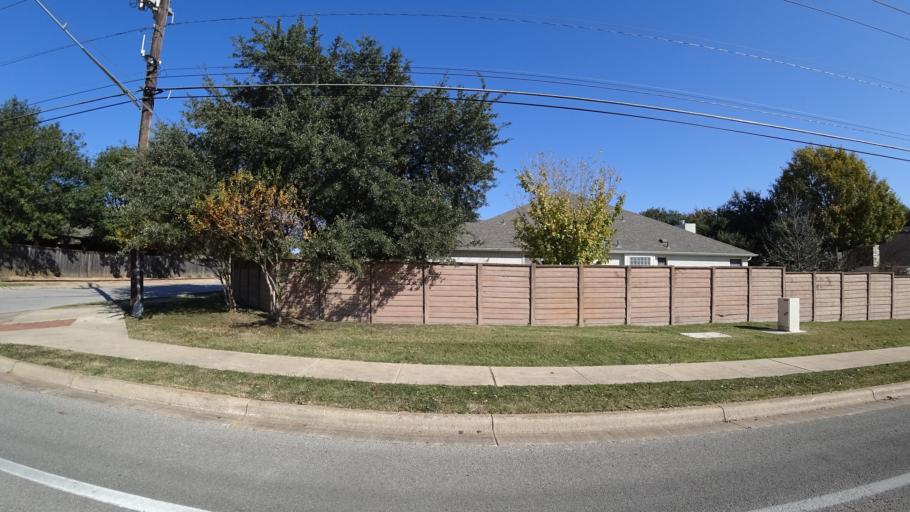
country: US
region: Texas
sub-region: Travis County
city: Shady Hollow
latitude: 30.2192
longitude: -97.8551
